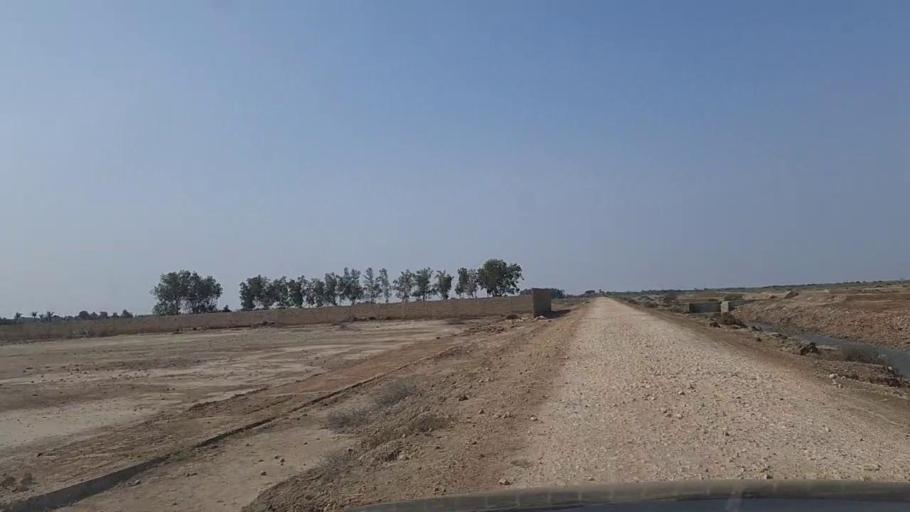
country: PK
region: Sindh
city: Gharo
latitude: 24.7019
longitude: 67.5906
